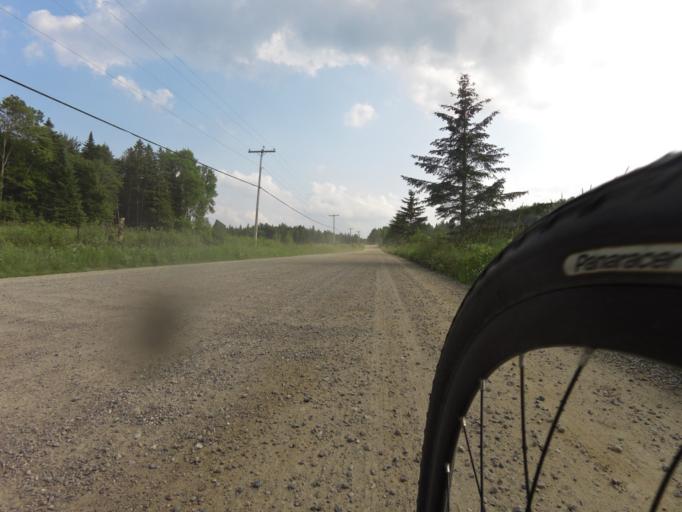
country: CA
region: Quebec
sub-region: Laurentides
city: Mont-Tremblant
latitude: 45.9552
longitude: -74.5933
